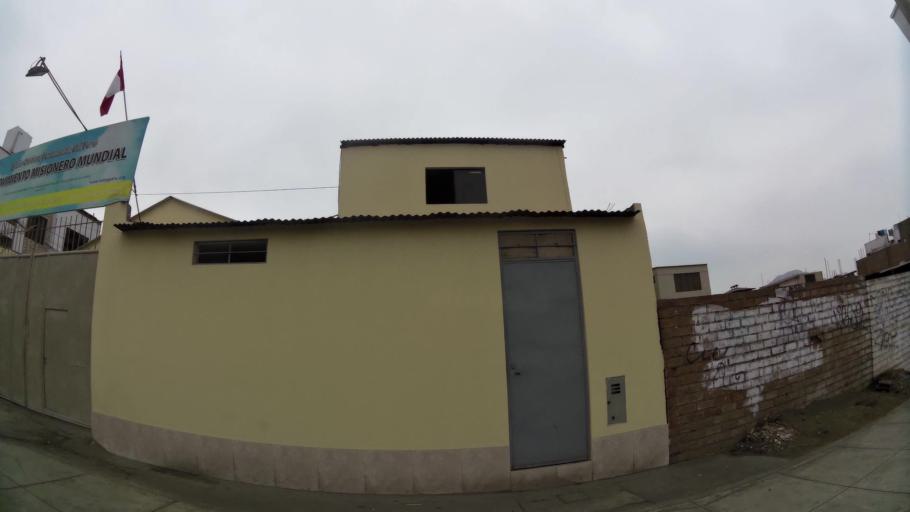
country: PE
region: Lima
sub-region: Lima
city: La Molina
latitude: -12.1034
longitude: -76.9419
